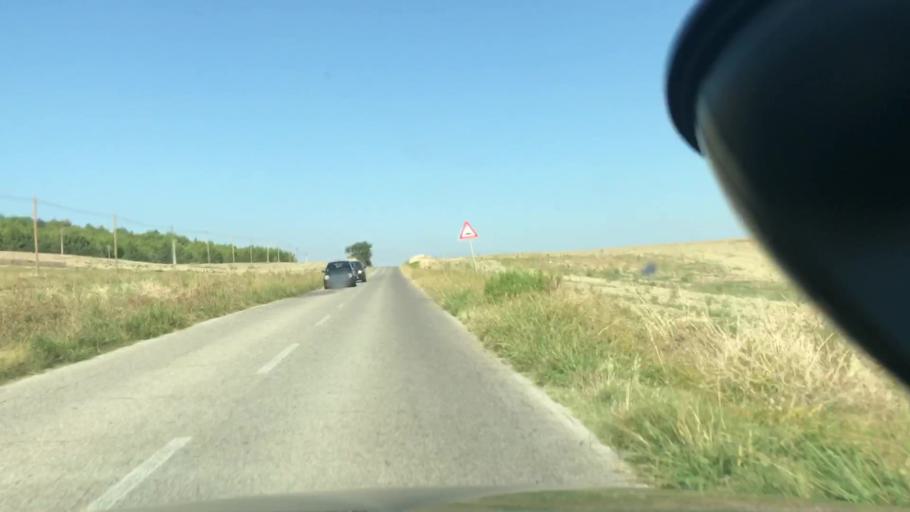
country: IT
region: Basilicate
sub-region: Provincia di Matera
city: La Martella
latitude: 40.6647
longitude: 16.4961
